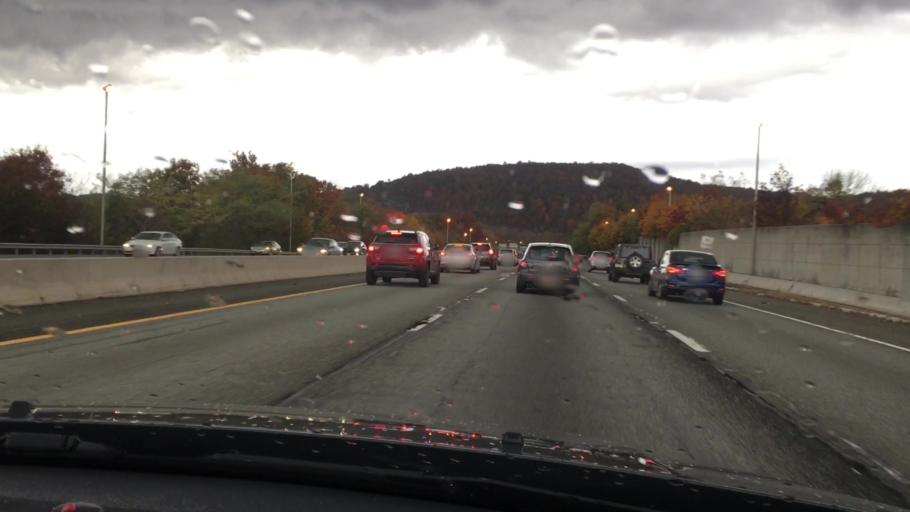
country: US
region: New Jersey
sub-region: Bergen County
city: Oakland
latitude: 41.0278
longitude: -74.2388
